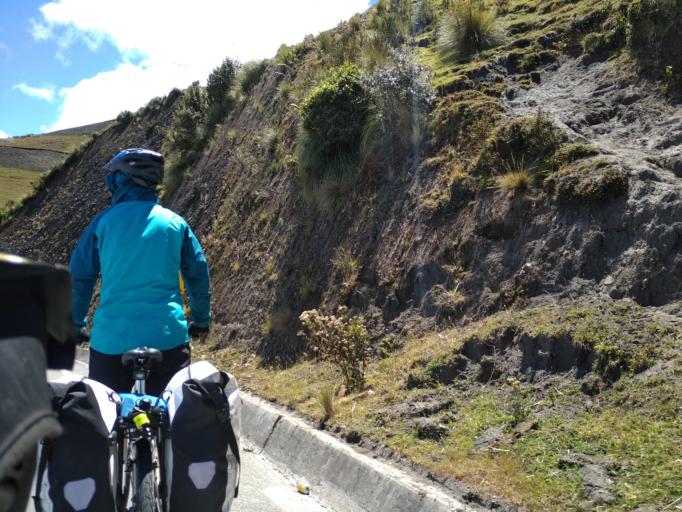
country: EC
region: Cotopaxi
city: Pujili
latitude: -0.9901
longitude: -78.9587
